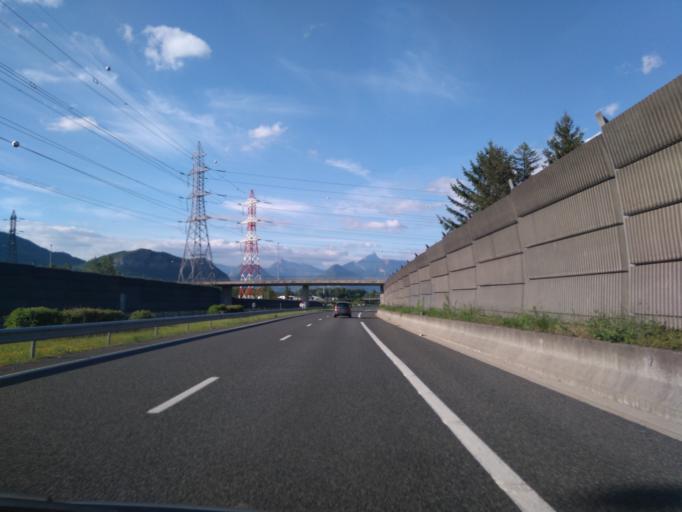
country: FR
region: Rhone-Alpes
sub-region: Departement de l'Isere
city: Allieres-et-Risset
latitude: 45.1068
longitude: 5.6785
